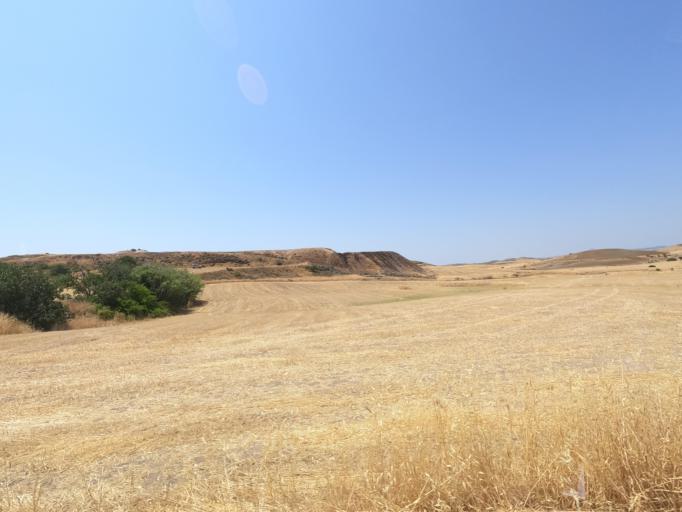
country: CY
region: Larnaka
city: Troulloi
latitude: 35.0308
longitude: 33.6404
